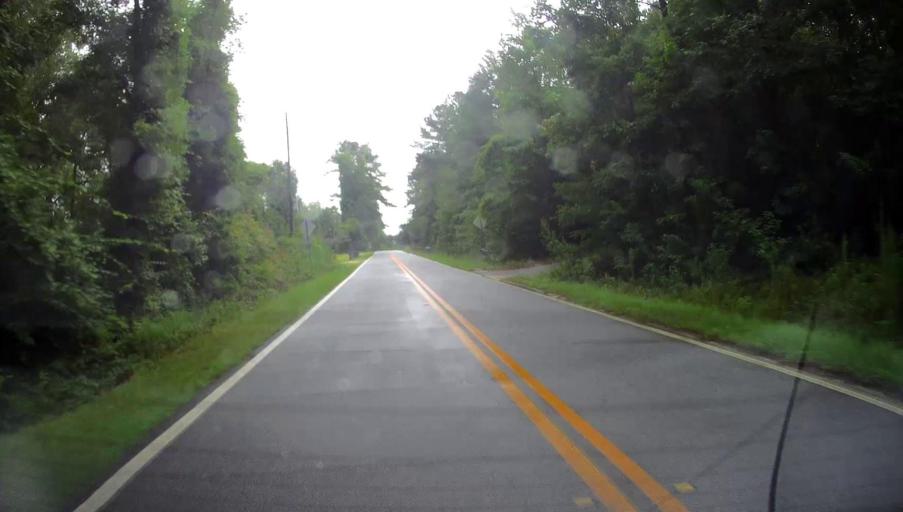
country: US
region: Georgia
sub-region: Bibb County
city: West Point
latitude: 32.7865
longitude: -83.7692
